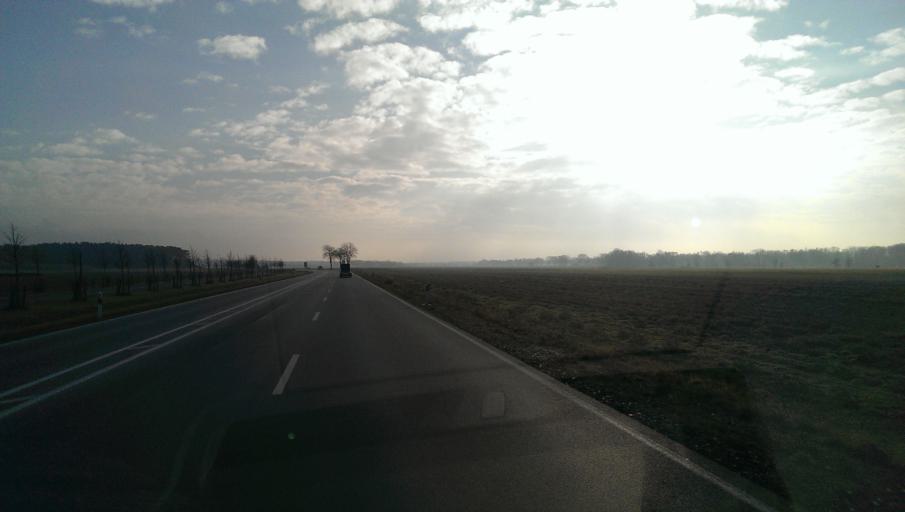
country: DE
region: Brandenburg
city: Herzberg
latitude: 51.6760
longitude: 13.2649
